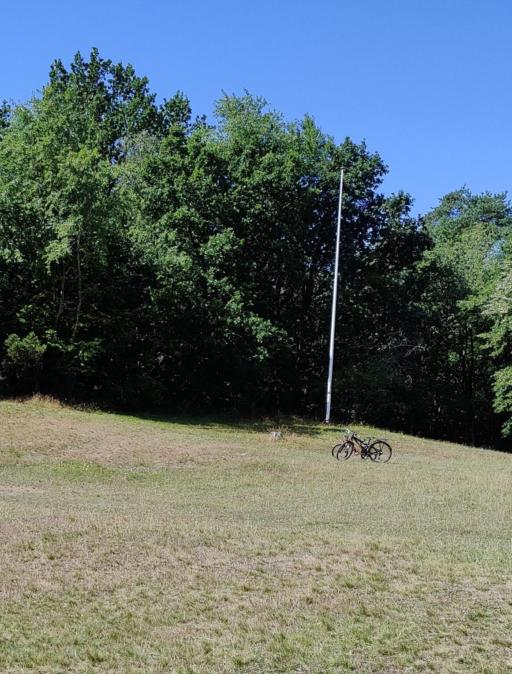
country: DK
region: South Denmark
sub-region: Middelfart Kommune
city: Ejby
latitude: 55.3855
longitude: 9.9396
